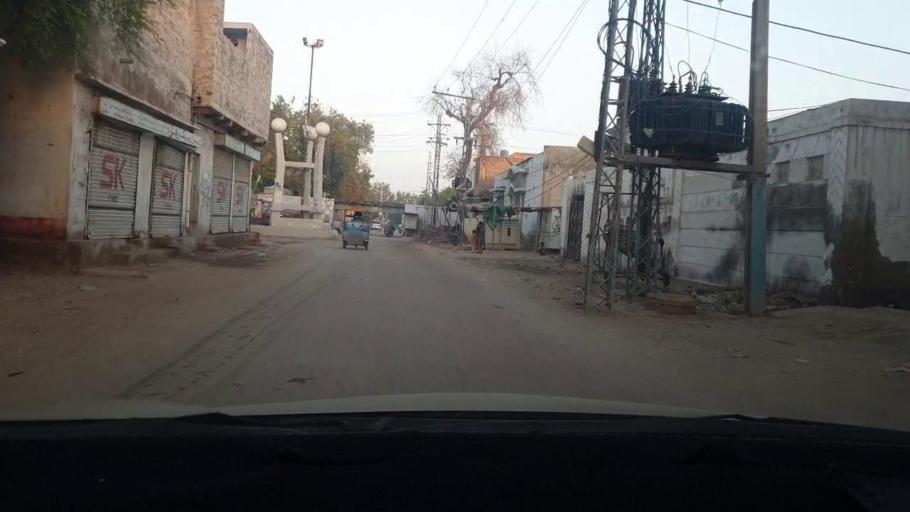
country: PK
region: Sindh
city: Larkana
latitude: 27.5571
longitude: 68.2135
